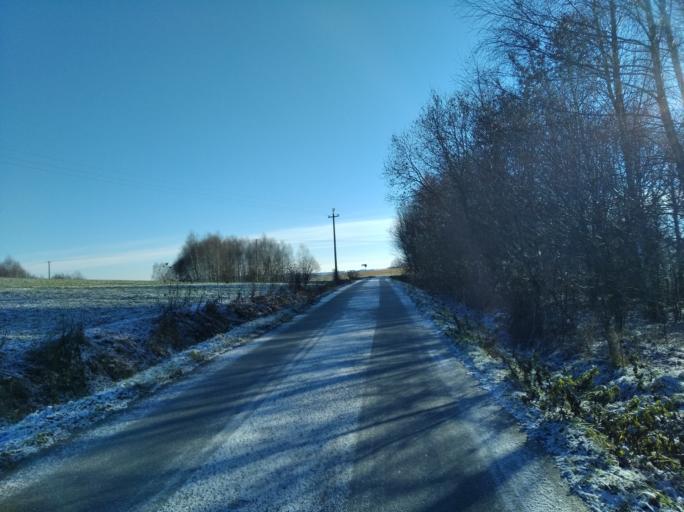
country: PL
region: Subcarpathian Voivodeship
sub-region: Powiat strzyzowski
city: Czudec
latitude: 49.9450
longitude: 21.7663
